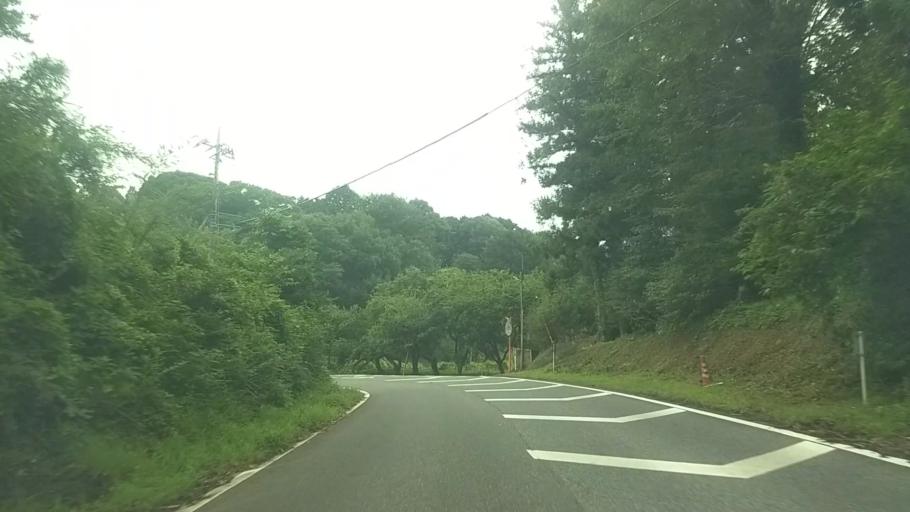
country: JP
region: Chiba
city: Kimitsu
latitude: 35.2297
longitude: 140.0098
